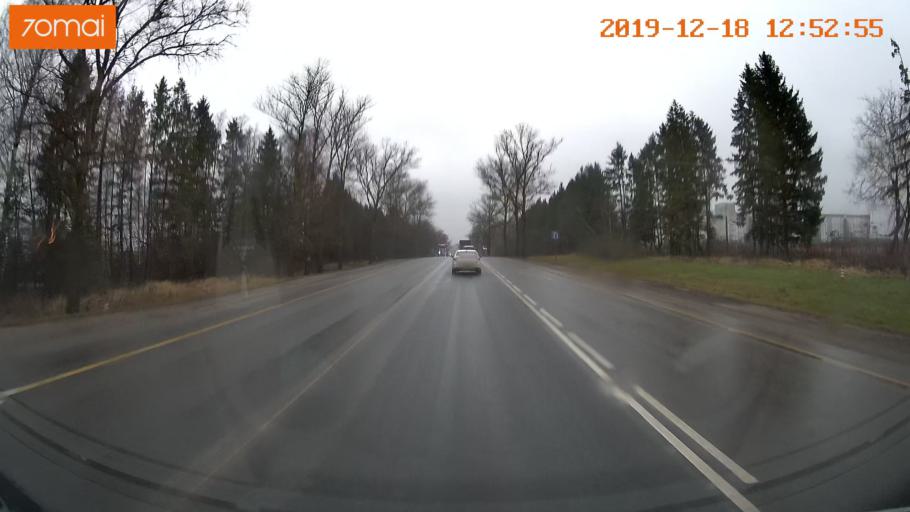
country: RU
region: Moskovskaya
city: Klin
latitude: 56.3149
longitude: 36.6906
